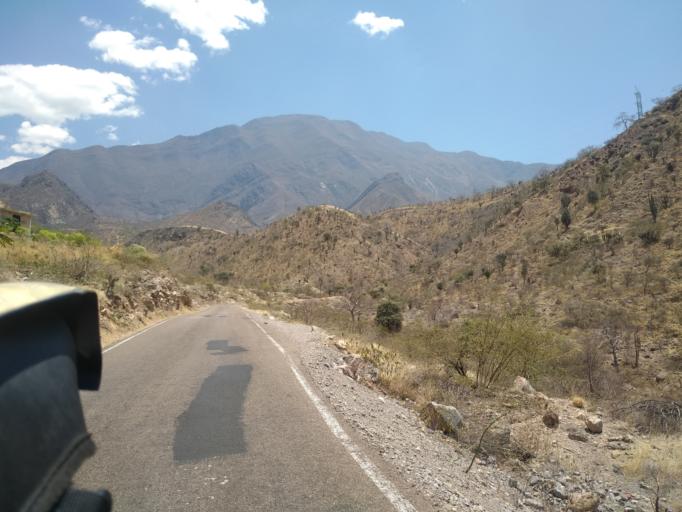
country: PE
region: Amazonas
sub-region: Provincia de Chachapoyas
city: Balsas
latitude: -6.8528
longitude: -78.0331
